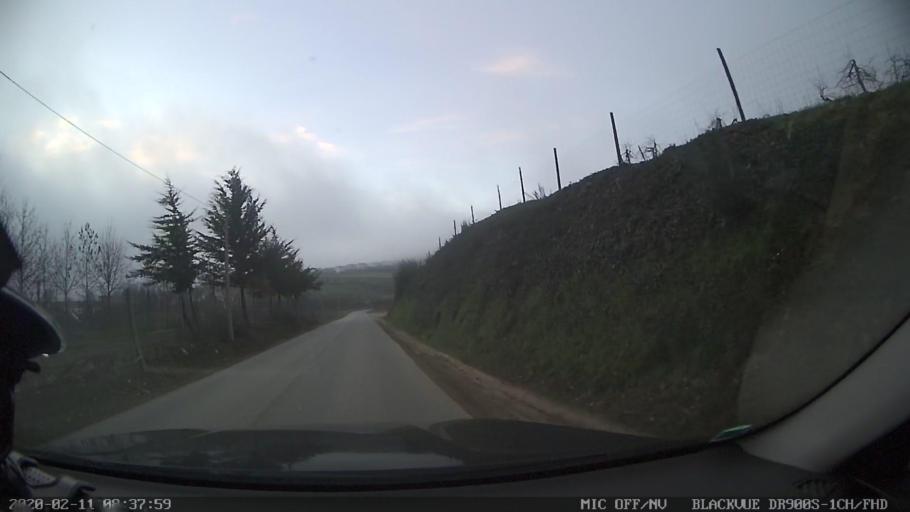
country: PT
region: Vila Real
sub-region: Sabrosa
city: Sabrosa
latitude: 41.2521
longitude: -7.5854
